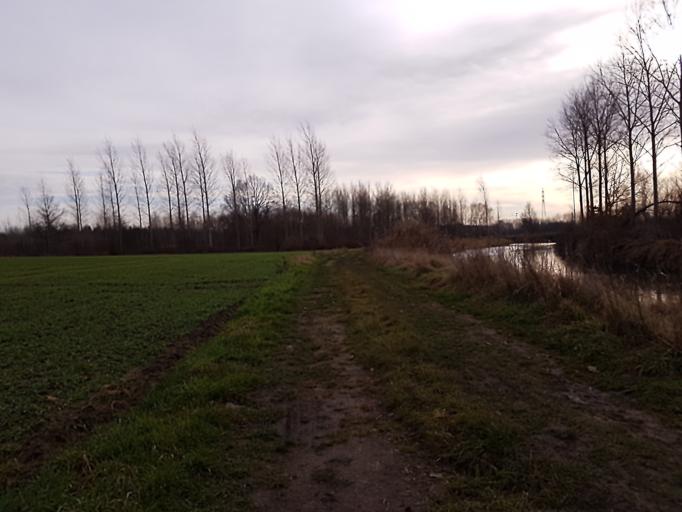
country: BE
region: Flanders
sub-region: Provincie Vlaams-Brabant
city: Rotselaar
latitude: 50.9376
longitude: 4.7115
